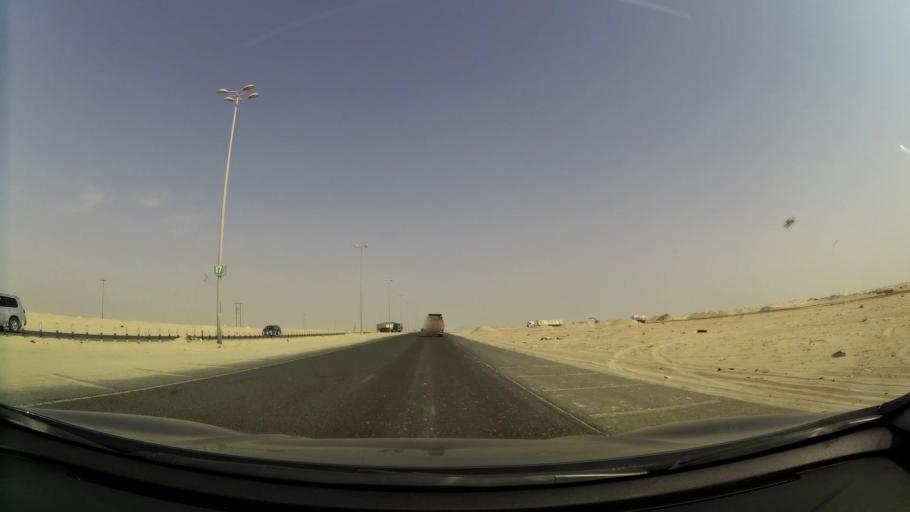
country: KW
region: Al Ahmadi
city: Al Wafrah
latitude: 28.8173
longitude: 48.0465
